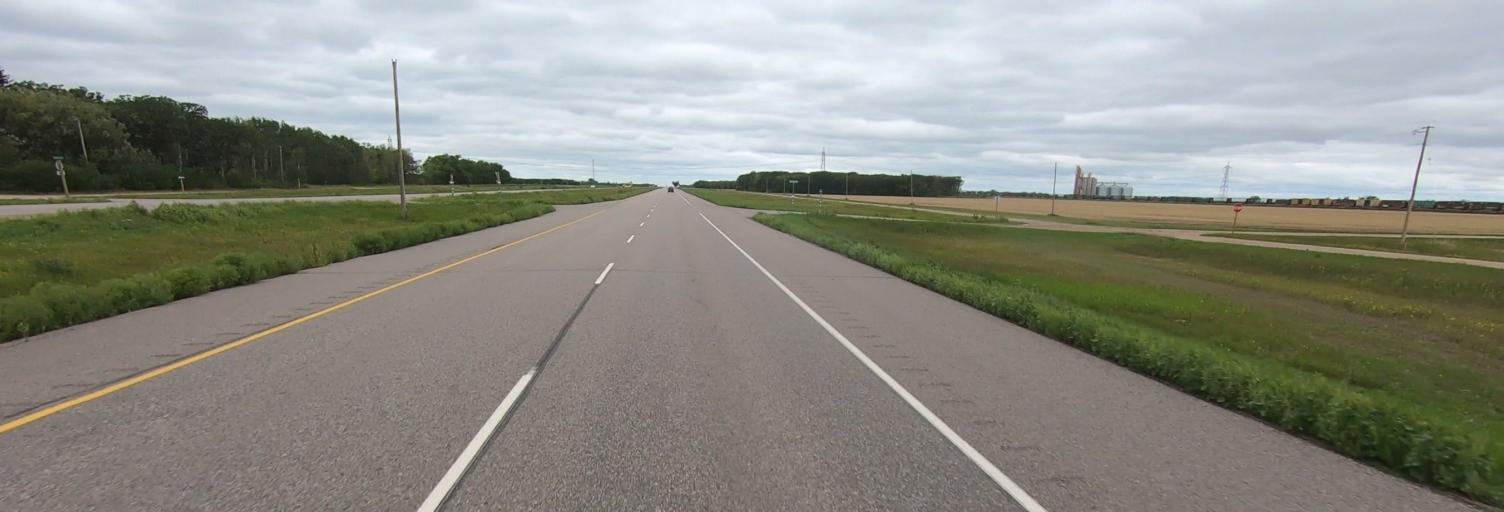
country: CA
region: Manitoba
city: Portage la Prairie
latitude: 49.9752
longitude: -98.5362
